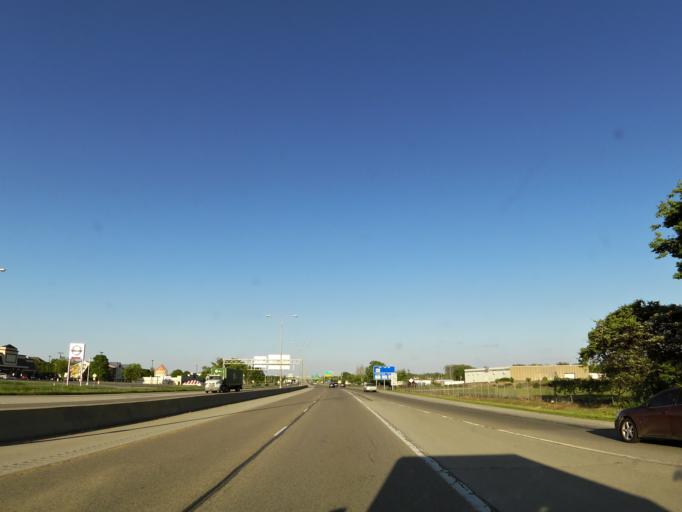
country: US
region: Illinois
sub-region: Champaign County
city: Champaign
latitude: 40.1346
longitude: -88.2550
